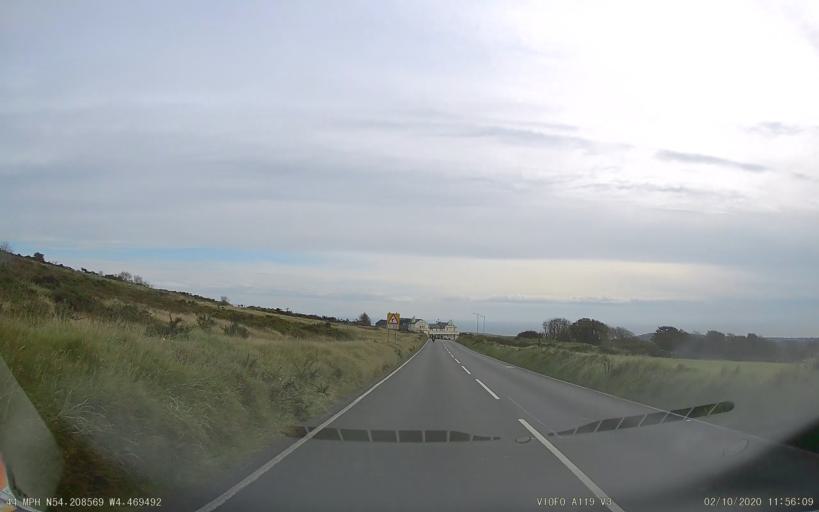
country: IM
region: Douglas
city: Douglas
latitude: 54.2086
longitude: -4.4696
